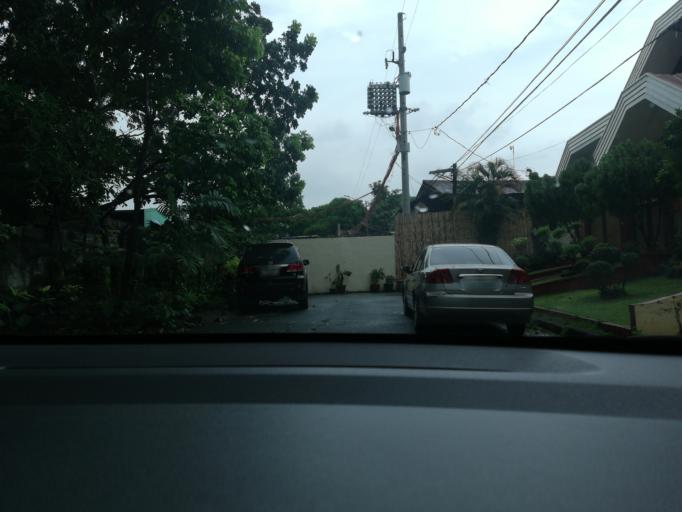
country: PH
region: Metro Manila
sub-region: Quezon City
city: Quezon City
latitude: 14.6804
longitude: 121.0776
